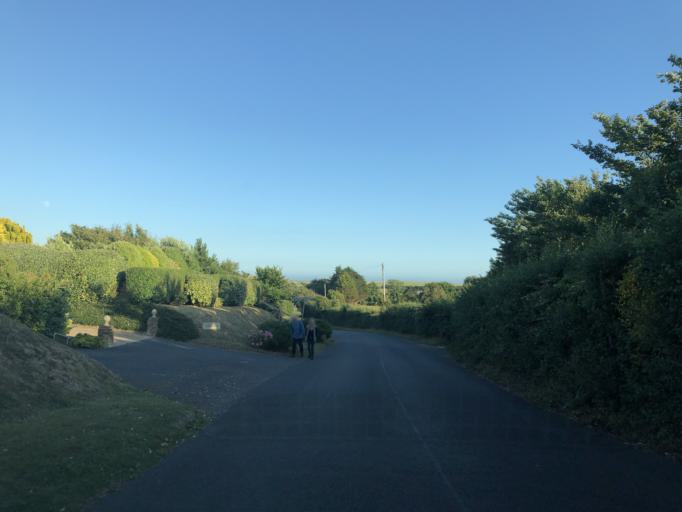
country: GB
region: England
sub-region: Isle of Wight
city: Shalfleet
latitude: 50.6411
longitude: -1.4019
